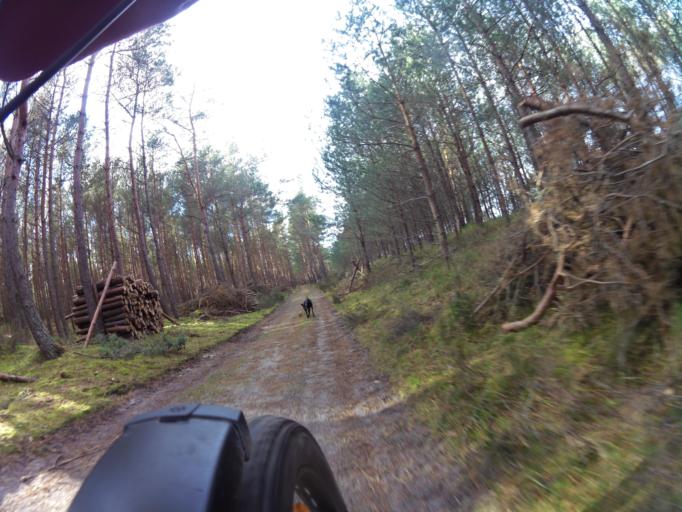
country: PL
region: Pomeranian Voivodeship
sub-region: Powiat wejherowski
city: Choczewo
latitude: 54.8055
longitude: 17.7974
